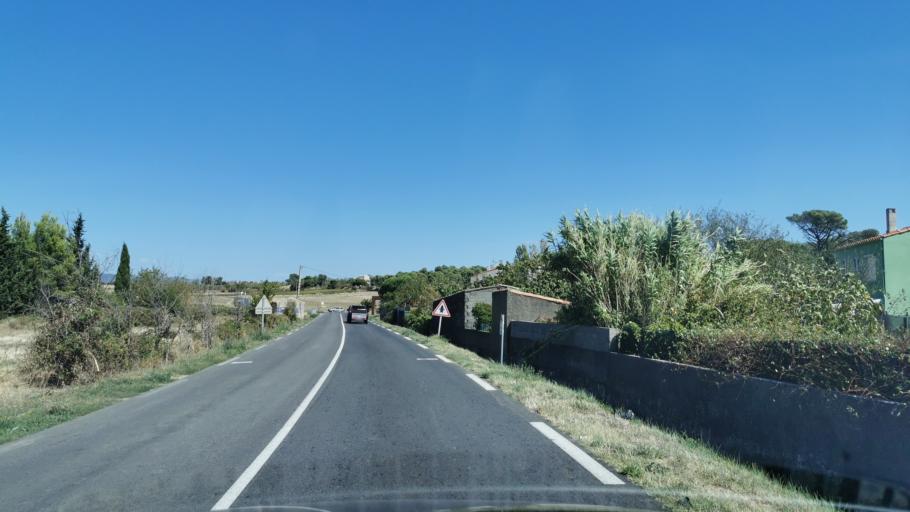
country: FR
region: Languedoc-Roussillon
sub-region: Departement de l'Aude
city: Conques-sur-Orbiel
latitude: 43.2600
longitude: 2.4176
